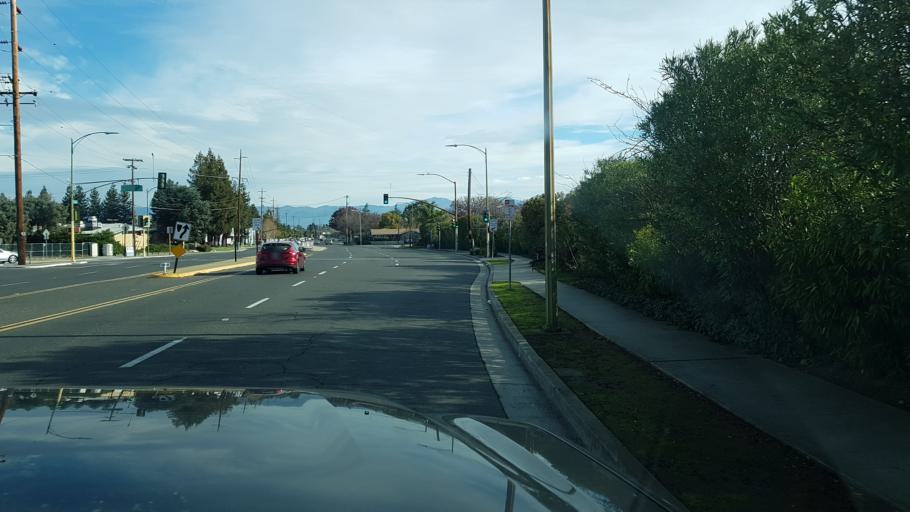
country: US
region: California
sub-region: Santa Clara County
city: Cambrian Park
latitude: 37.2453
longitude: -121.8881
